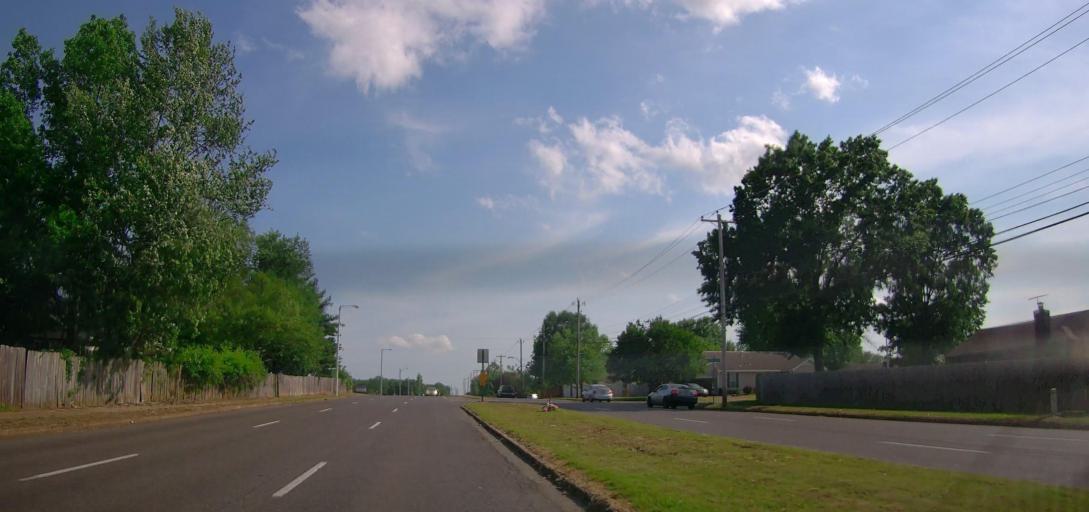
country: US
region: Mississippi
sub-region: De Soto County
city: Olive Branch
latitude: 35.0272
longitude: -89.8482
